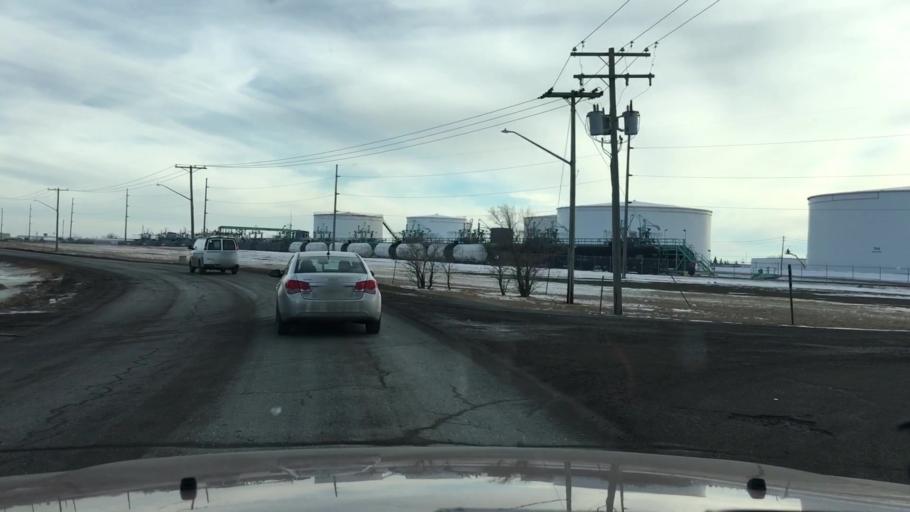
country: CA
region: Saskatchewan
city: Regina
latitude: 50.4829
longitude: -104.5800
